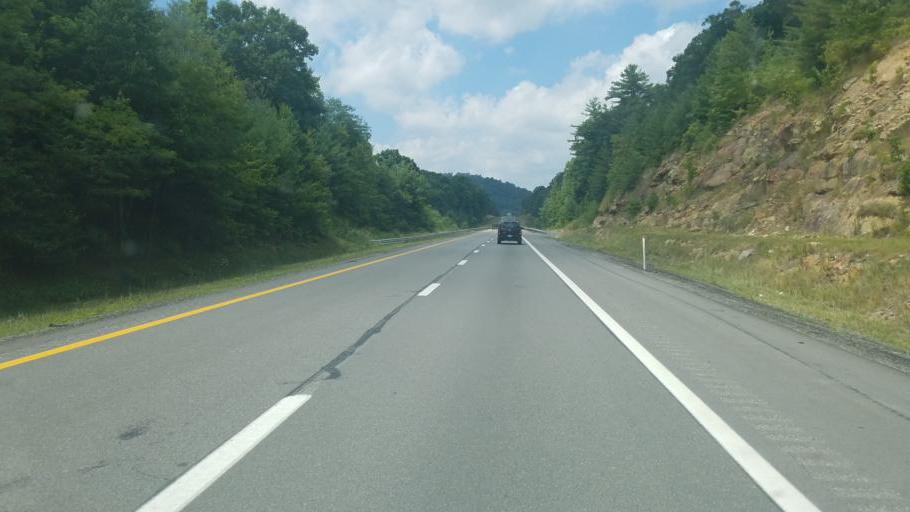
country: US
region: West Virginia
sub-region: Raleigh County
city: Shady Spring
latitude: 37.7009
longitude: -81.1402
